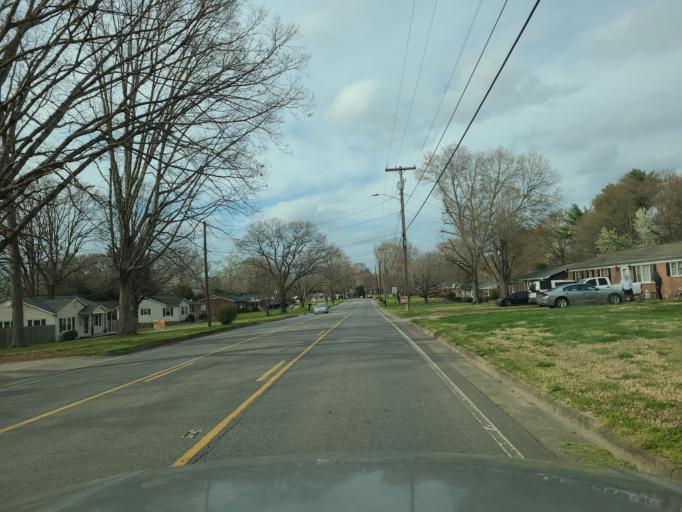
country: US
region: North Carolina
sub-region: Cleveland County
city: Shelby
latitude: 35.2803
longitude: -81.5625
